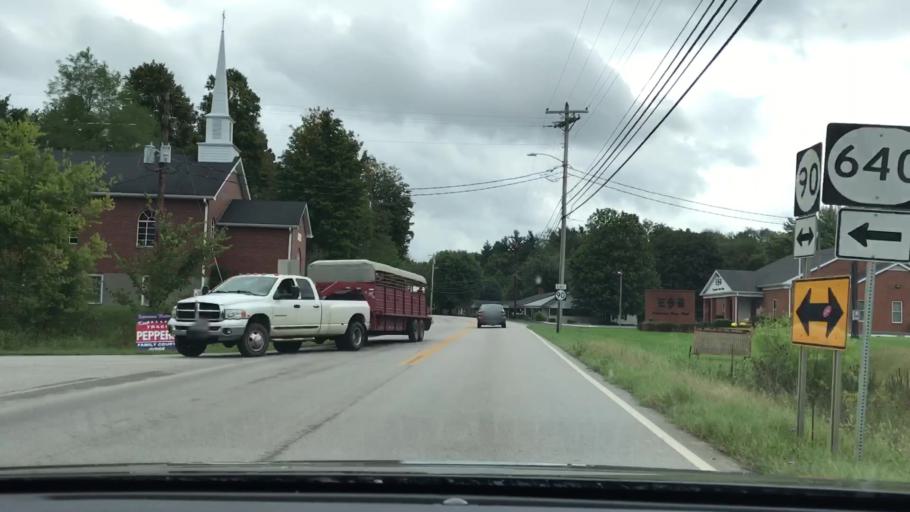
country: US
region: Kentucky
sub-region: Metcalfe County
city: Edmonton
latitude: 36.8848
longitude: -85.7051
